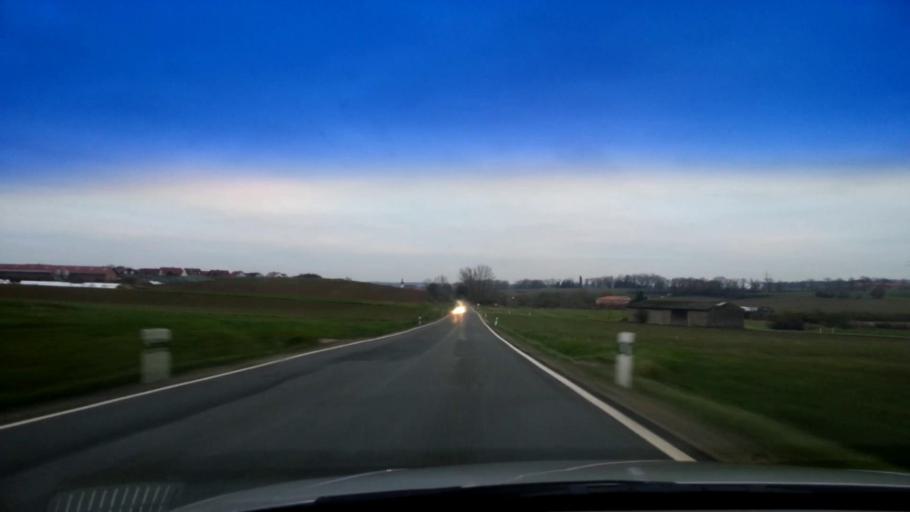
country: DE
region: Bavaria
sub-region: Upper Franconia
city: Pommersfelden
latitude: 49.7799
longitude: 10.7971
